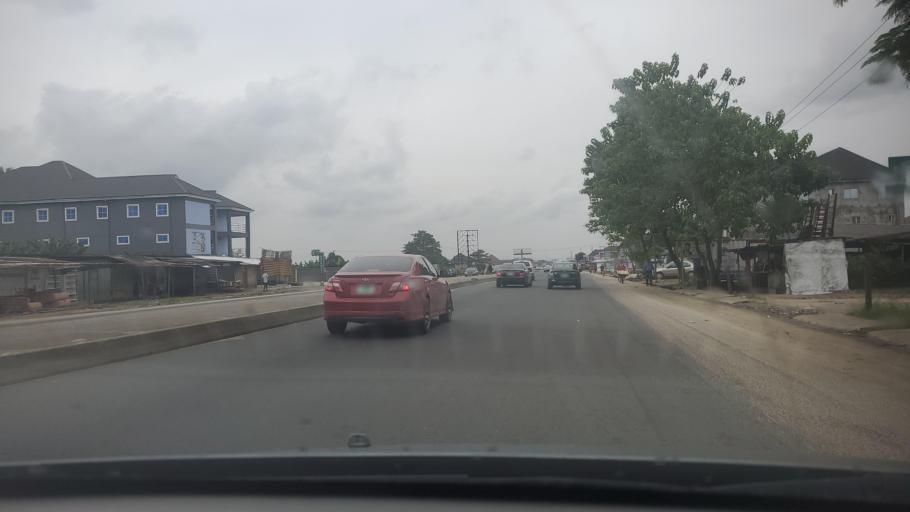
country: NG
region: Rivers
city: Port Harcourt
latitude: 4.8702
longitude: 6.9726
